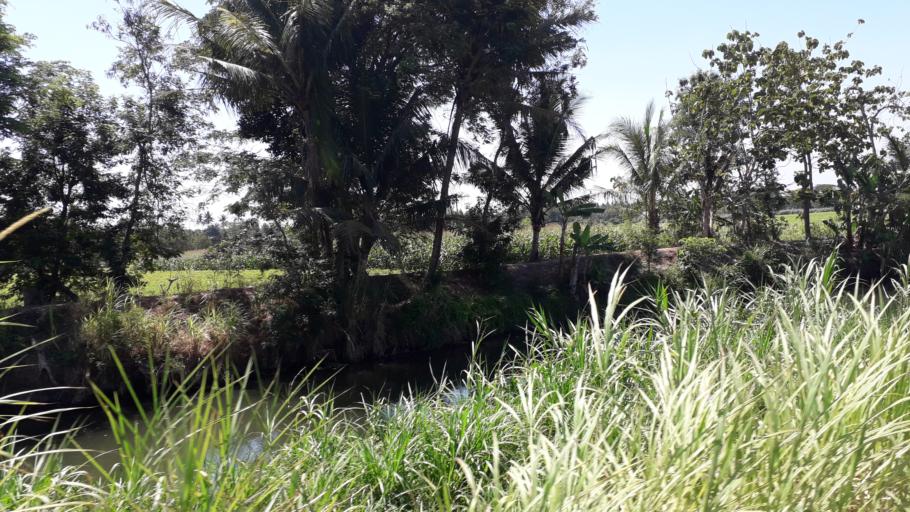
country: ID
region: Daerah Istimewa Yogyakarta
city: Pundong
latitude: -7.9490
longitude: 110.3281
